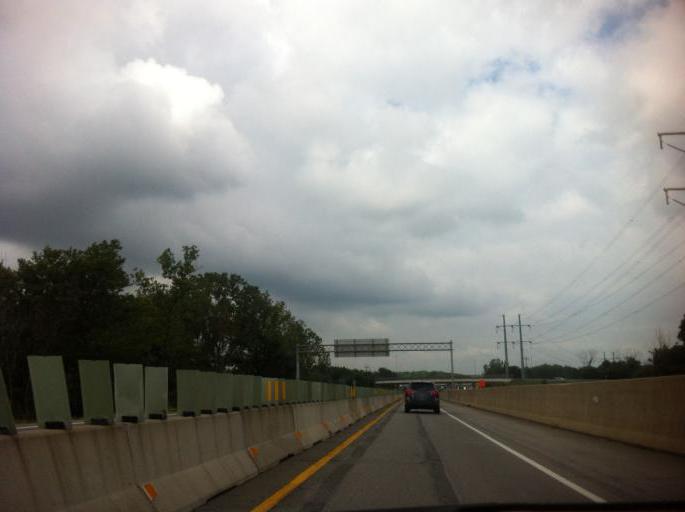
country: US
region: Ohio
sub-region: Cuyahoga County
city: Strongsville
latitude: 41.3304
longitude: -81.8088
